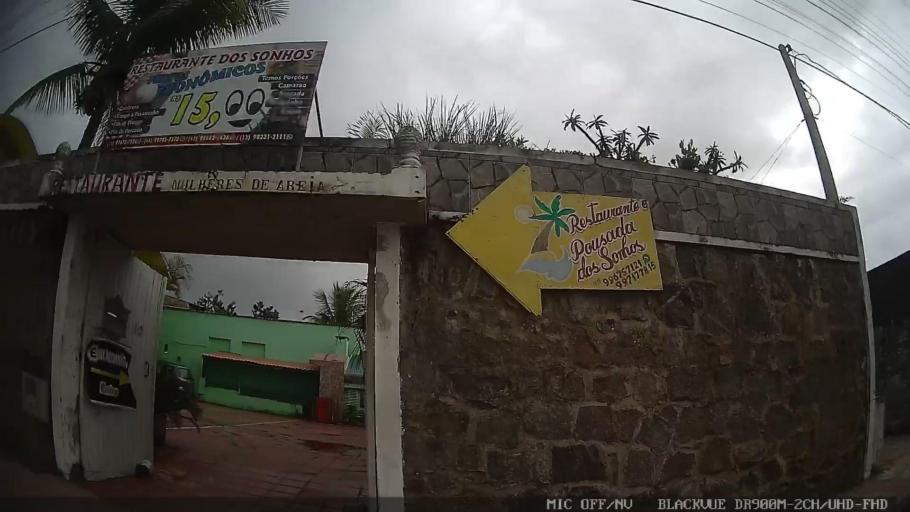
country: BR
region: Sao Paulo
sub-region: Itanhaem
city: Itanhaem
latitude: -24.1927
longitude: -46.7951
